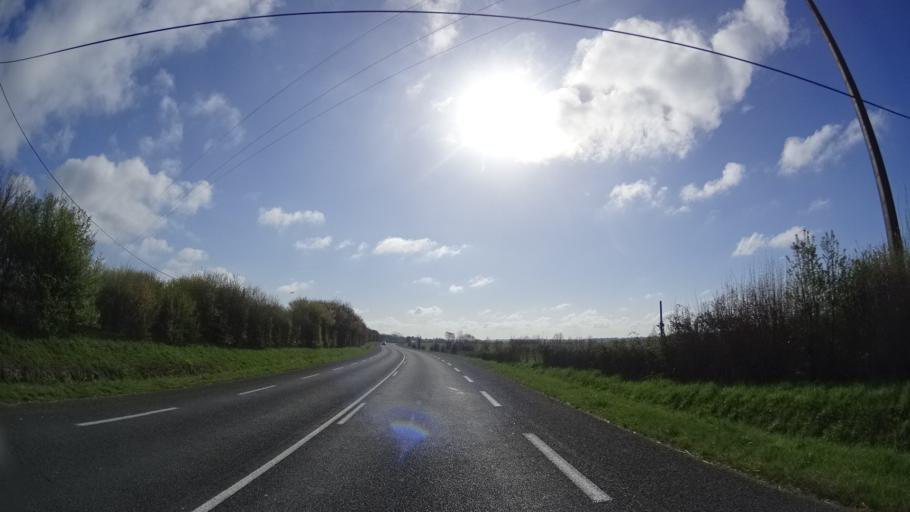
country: FR
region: Pays de la Loire
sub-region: Departement de Maine-et-Loire
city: Pouance
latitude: 47.7685
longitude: -1.2242
